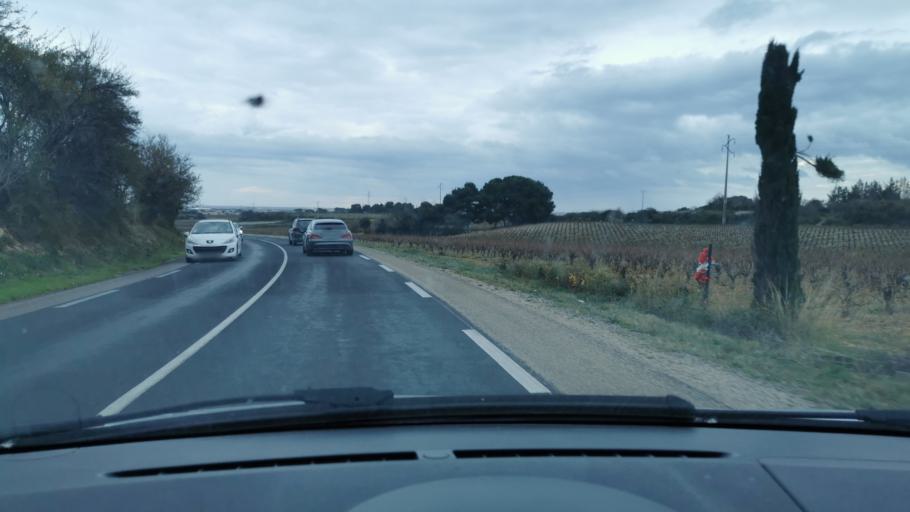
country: FR
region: Languedoc-Roussillon
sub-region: Departement de l'Herault
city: Frontignan
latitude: 43.4481
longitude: 3.7224
